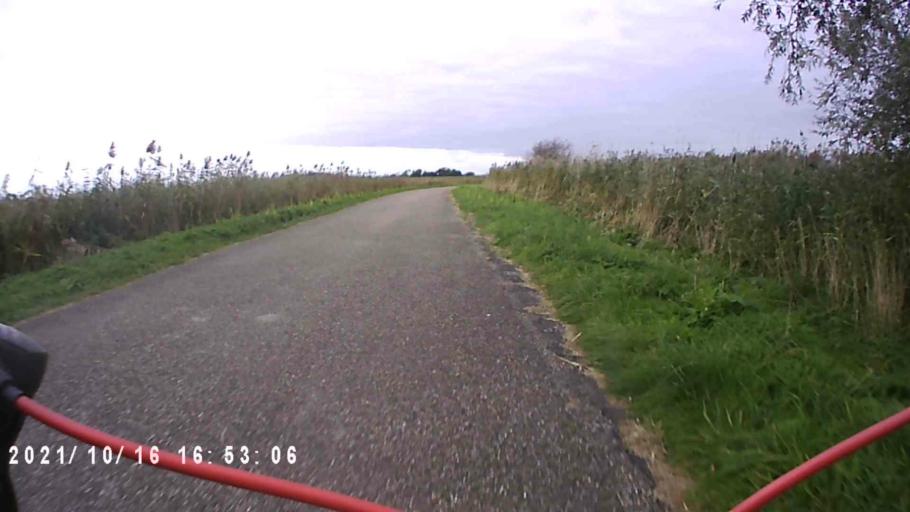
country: NL
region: Friesland
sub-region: Gemeente Dongeradeel
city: Anjum
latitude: 53.3533
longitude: 6.1513
